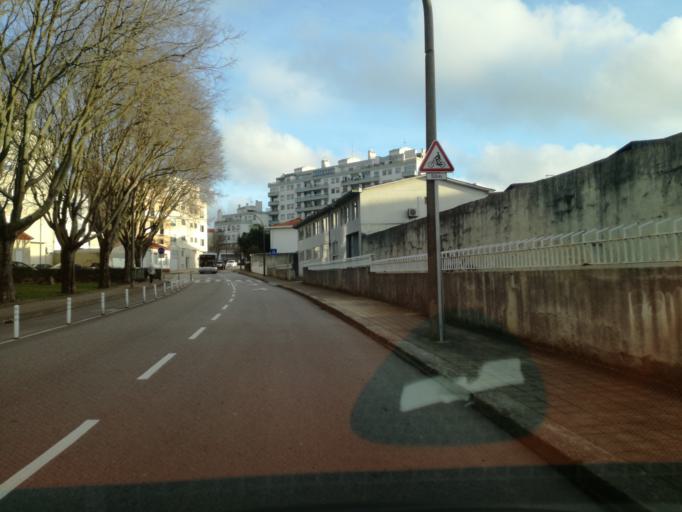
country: PT
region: Porto
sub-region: Matosinhos
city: Senhora da Hora
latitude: 41.1689
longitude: -8.6313
